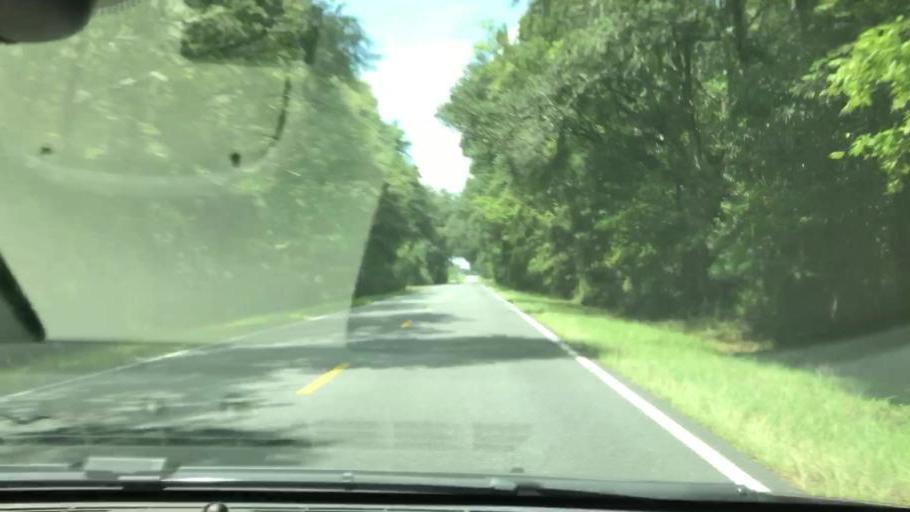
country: US
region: Florida
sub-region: Jackson County
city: Malone
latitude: 30.9463
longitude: -85.1183
